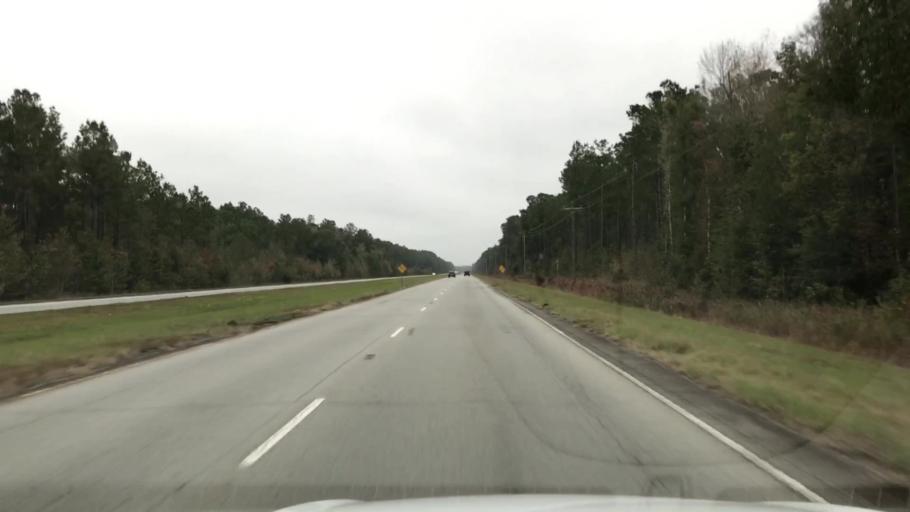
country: US
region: South Carolina
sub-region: Charleston County
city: Awendaw
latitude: 33.0068
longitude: -79.6406
